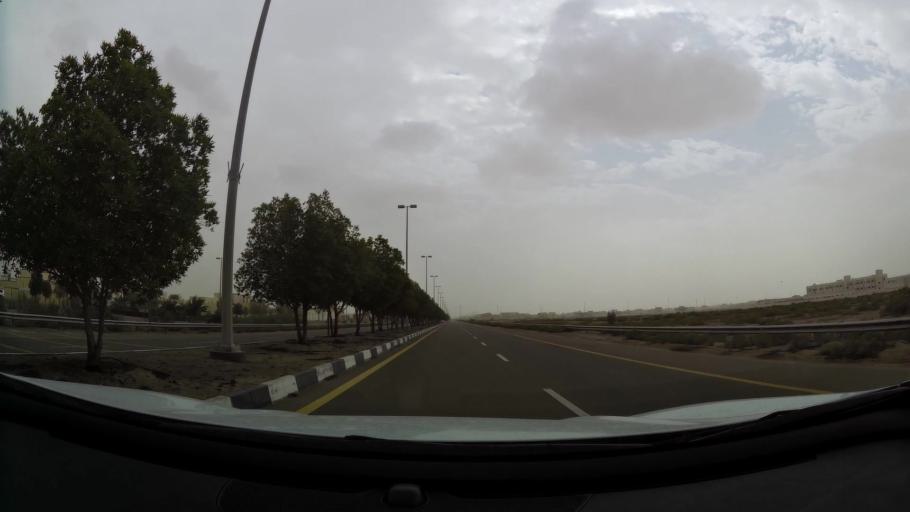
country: AE
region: Abu Dhabi
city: Abu Dhabi
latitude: 24.3803
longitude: 54.6886
